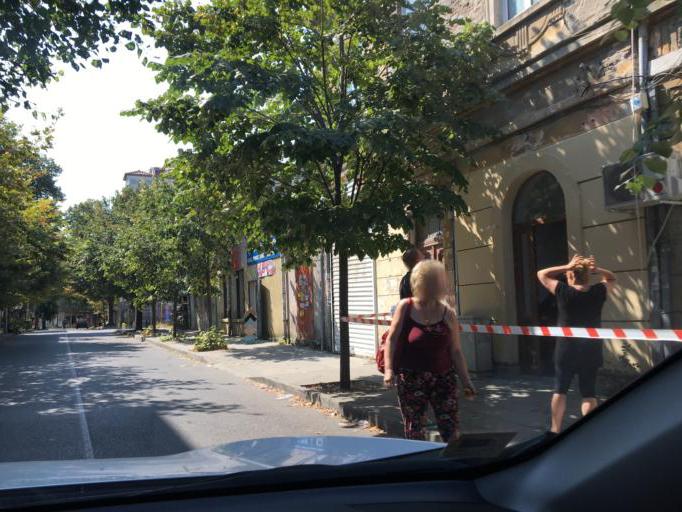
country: BG
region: Burgas
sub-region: Obshtina Burgas
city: Burgas
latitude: 42.4922
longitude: 27.4644
